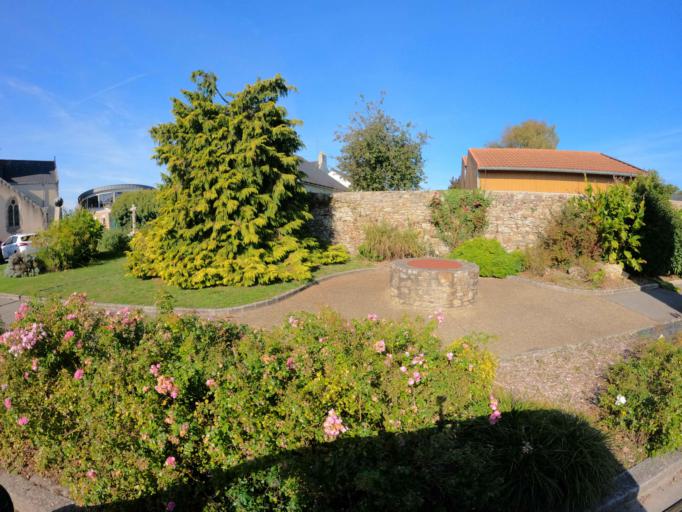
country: FR
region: Brittany
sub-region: Departement du Morbihan
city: Ferel
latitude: 47.5164
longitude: -2.3754
